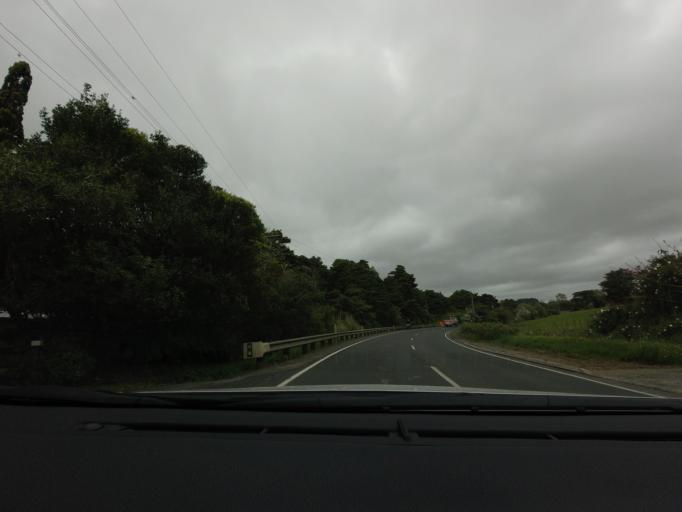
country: NZ
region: Auckland
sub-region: Auckland
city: Warkworth
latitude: -36.4054
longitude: 174.6318
